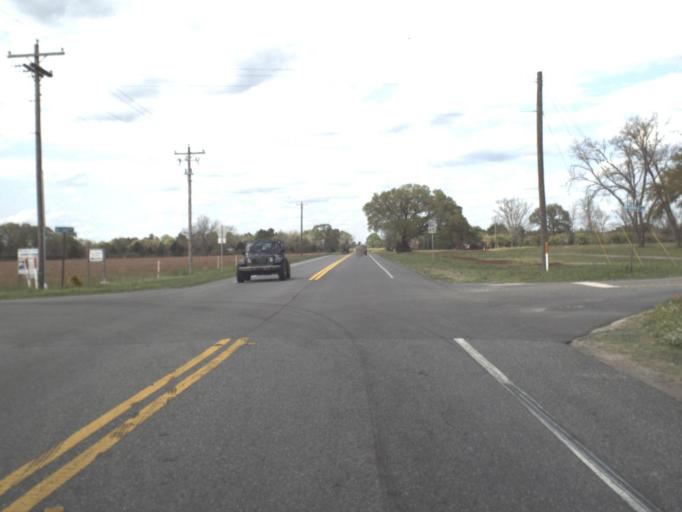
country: US
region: Florida
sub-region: Okaloosa County
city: Crestview
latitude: 30.8520
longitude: -86.5283
